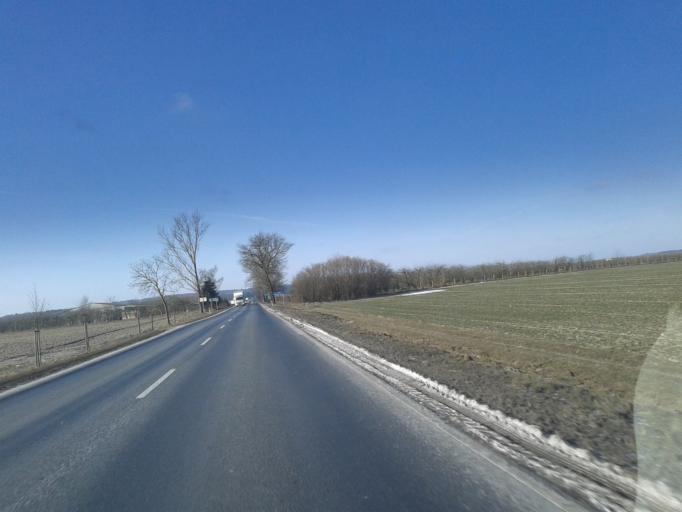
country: PL
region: Greater Poland Voivodeship
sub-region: Powiat pilski
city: Wysoka
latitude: 53.1394
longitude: 17.0793
